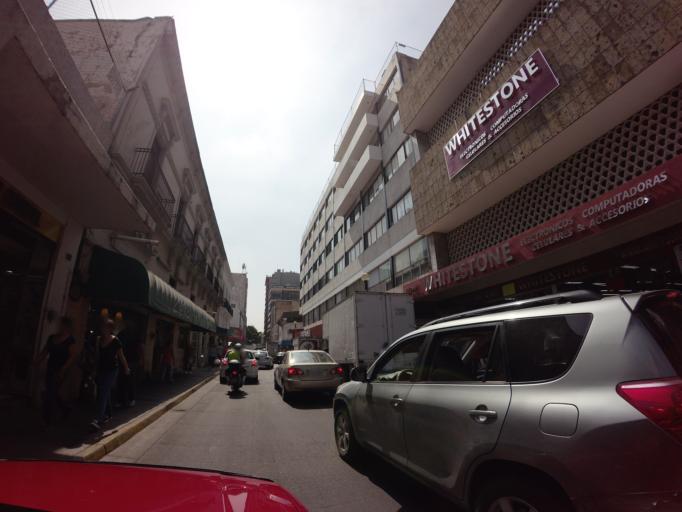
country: MX
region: Jalisco
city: Guadalajara
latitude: 20.6744
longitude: -103.3486
